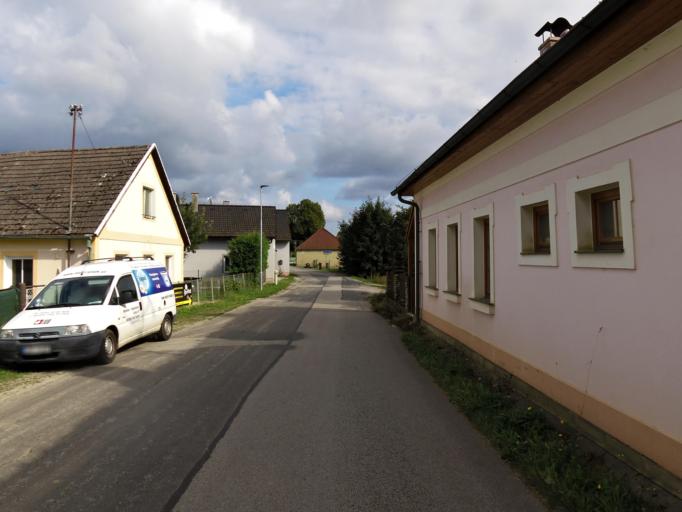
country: CZ
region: Jihocesky
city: Suchdol nad Luznici
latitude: 48.9058
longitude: 14.9108
